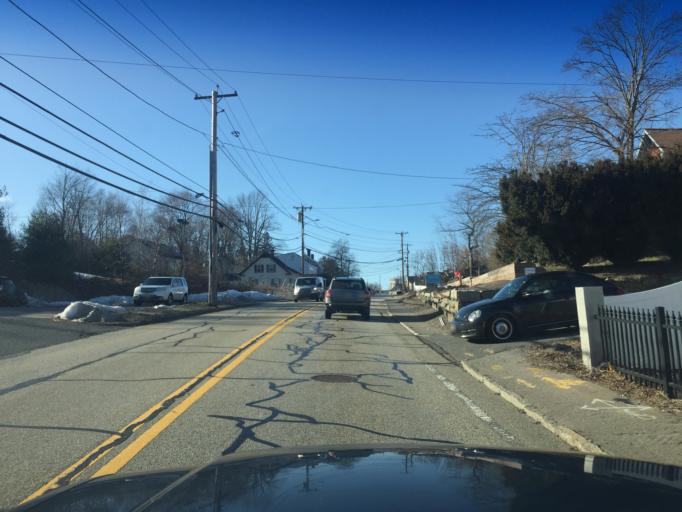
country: US
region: Massachusetts
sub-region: Norfolk County
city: Bellingham
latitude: 42.0846
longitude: -71.4715
